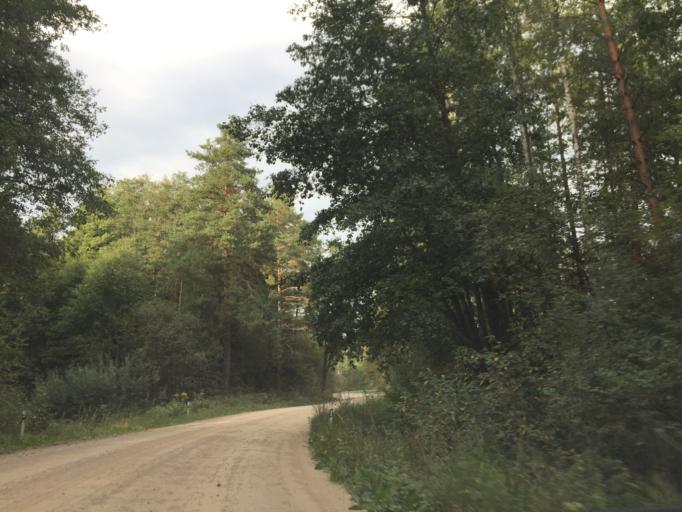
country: LV
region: Baldone
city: Baldone
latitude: 56.7954
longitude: 24.4375
